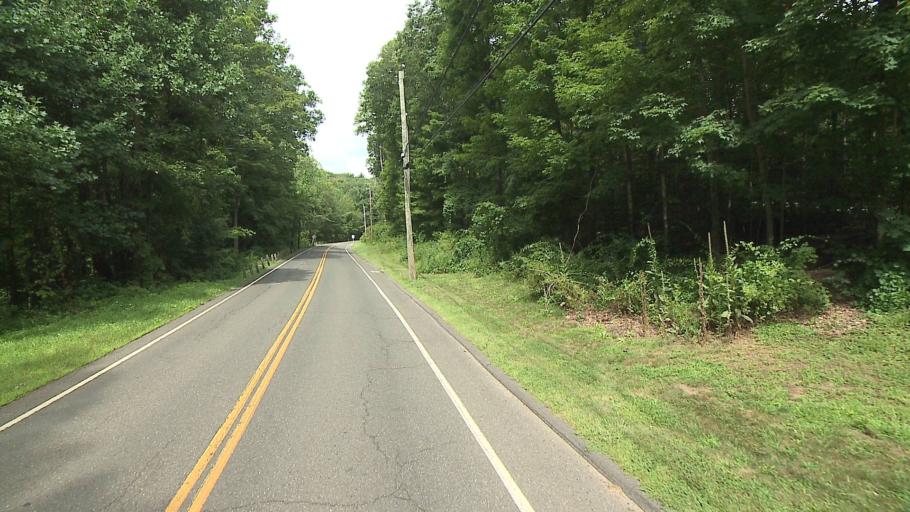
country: US
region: Connecticut
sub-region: Litchfield County
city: Woodbury
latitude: 41.5531
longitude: -73.2470
